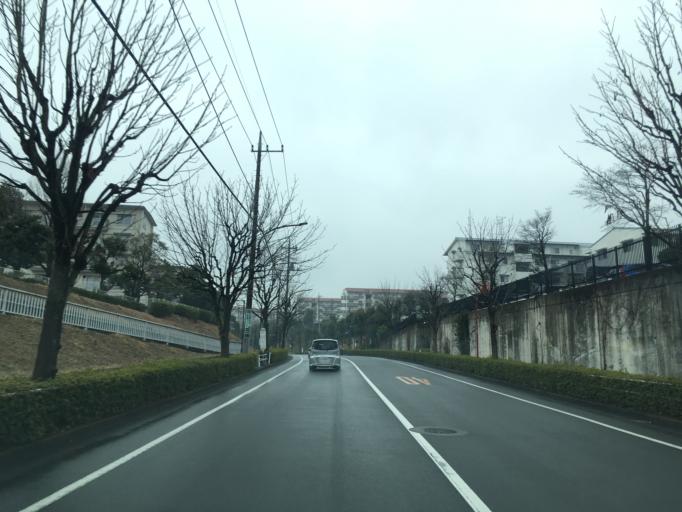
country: JP
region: Tokyo
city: Hino
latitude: 35.6140
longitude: 139.4281
